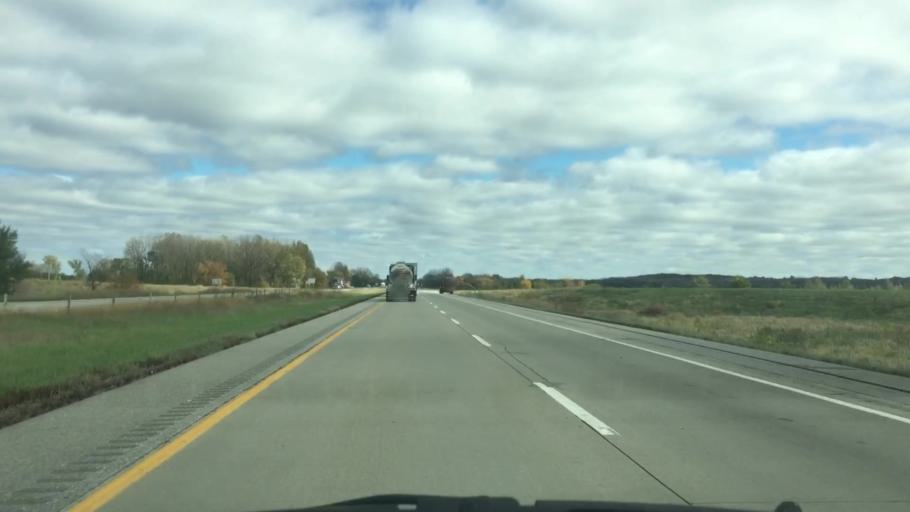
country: US
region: Iowa
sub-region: Jasper County
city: Colfax
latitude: 41.6922
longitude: -93.2460
